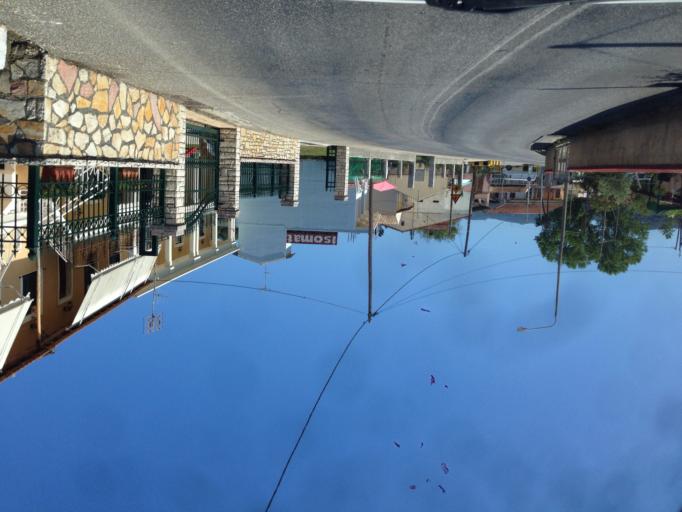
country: GR
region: Ionian Islands
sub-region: Nomos Kerkyras
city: Agios Georgis
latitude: 39.7520
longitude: 19.7156
